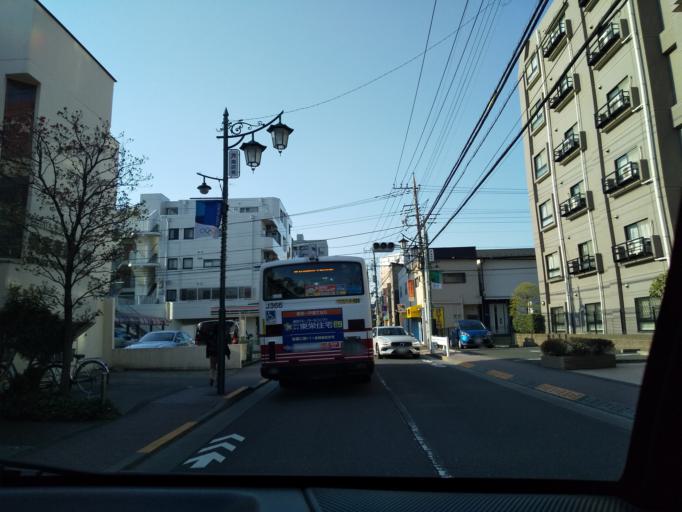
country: JP
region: Tokyo
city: Kokubunji
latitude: 35.7022
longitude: 139.4465
